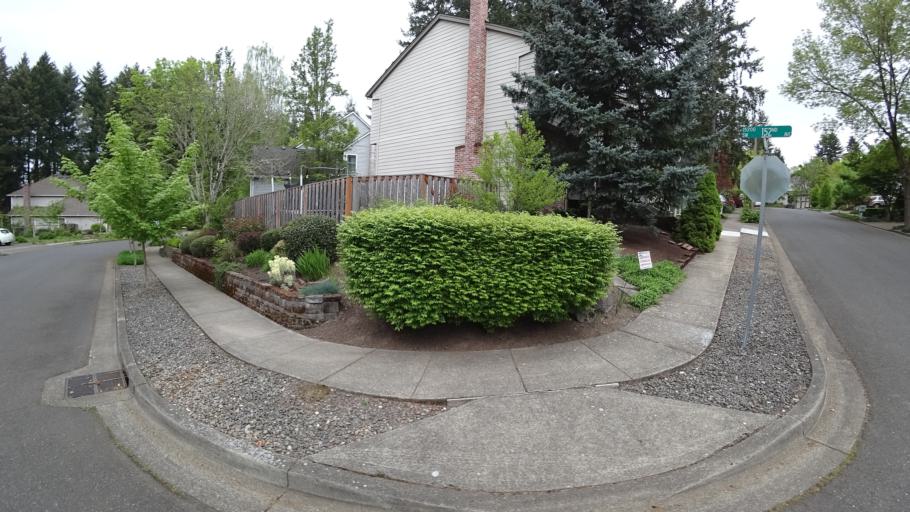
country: US
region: Oregon
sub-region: Washington County
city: Beaverton
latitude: 45.4606
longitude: -122.8332
